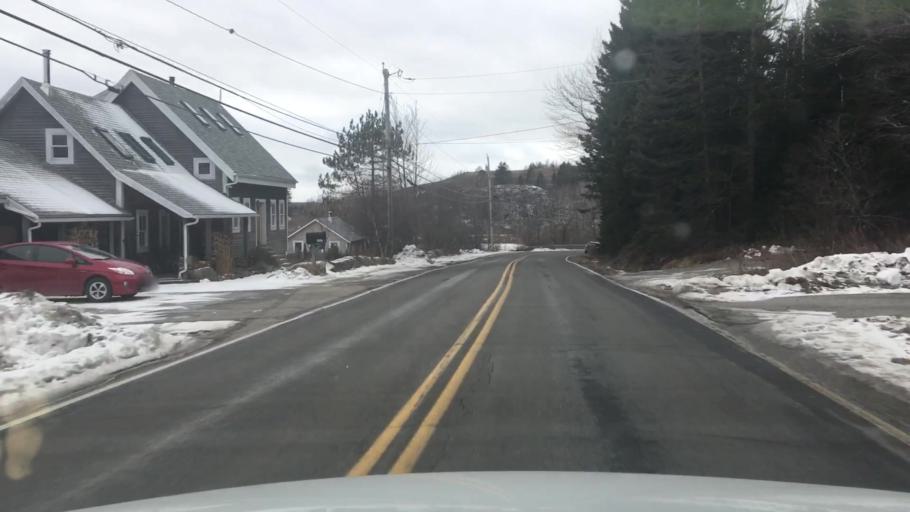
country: US
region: Maine
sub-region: Washington County
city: East Machias
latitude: 44.7238
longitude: -67.3822
